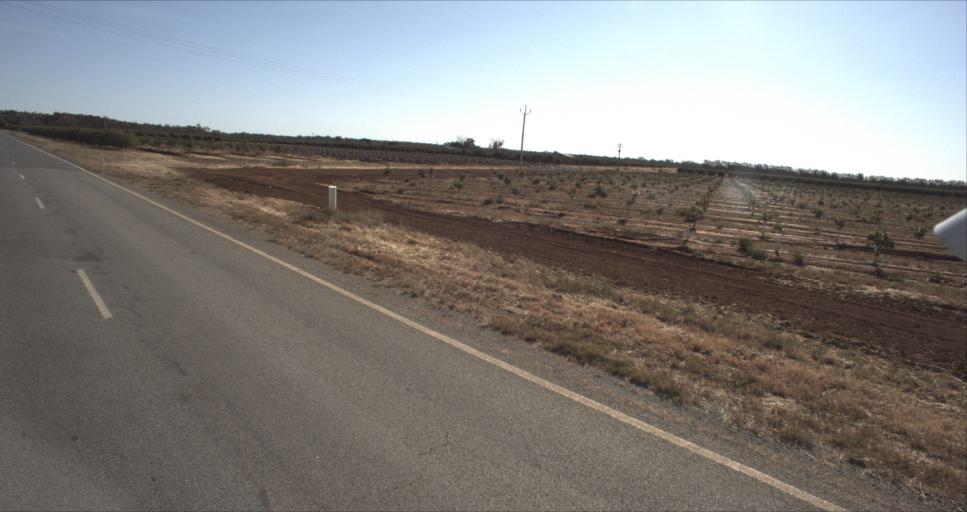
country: AU
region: New South Wales
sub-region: Leeton
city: Leeton
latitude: -34.6147
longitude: 146.4018
